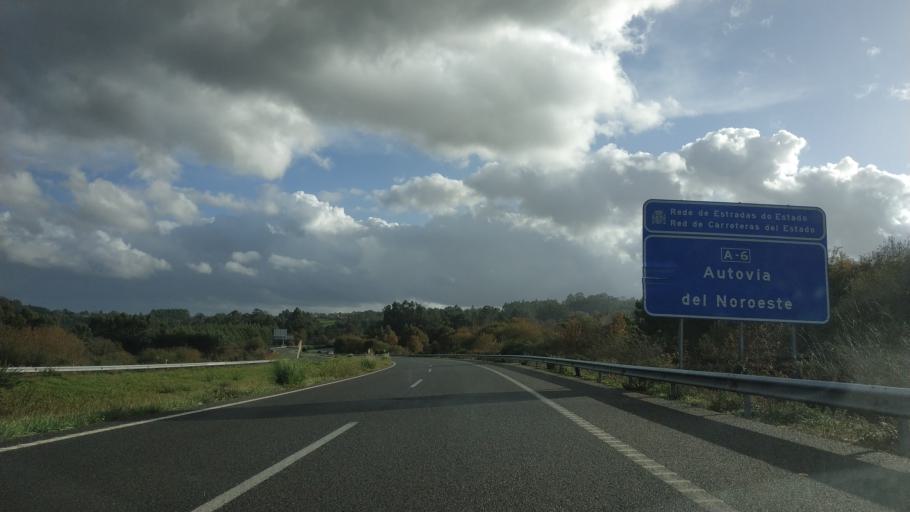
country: ES
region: Galicia
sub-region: Provincia da Coruna
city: Cambre
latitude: 43.2710
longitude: -8.3601
